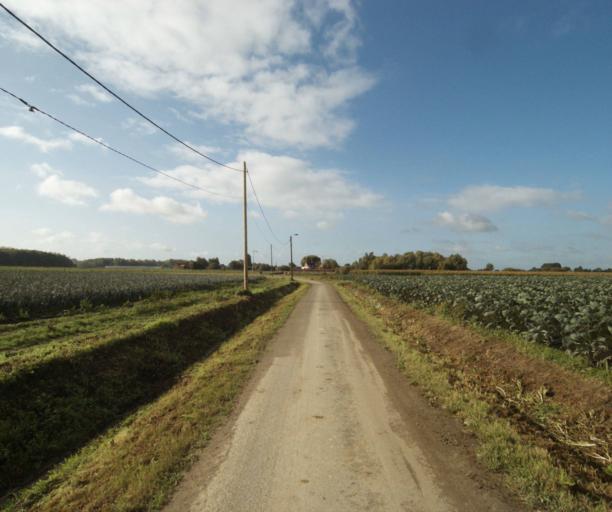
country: FR
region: Nord-Pas-de-Calais
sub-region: Departement du Nord
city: Verlinghem
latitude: 50.6913
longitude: 2.9848
